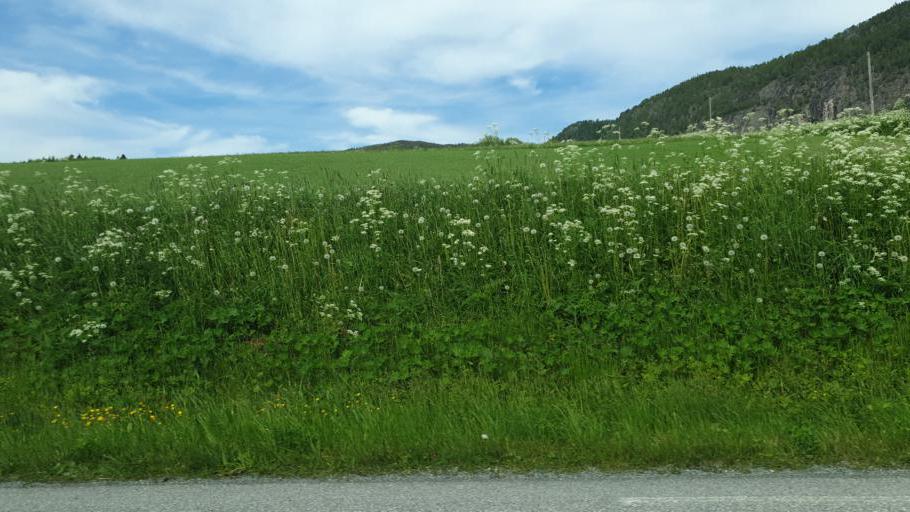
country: NO
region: Sor-Trondelag
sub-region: Trondheim
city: Trondheim
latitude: 63.5879
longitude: 10.4231
